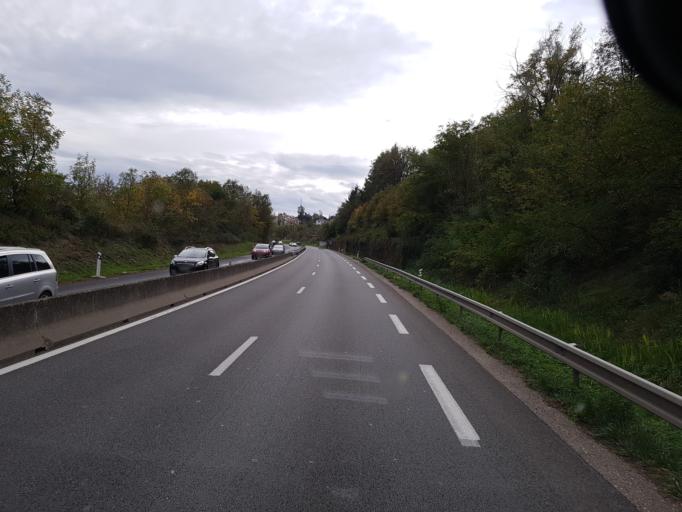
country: FR
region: Rhone-Alpes
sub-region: Departement de la Loire
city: Saint-Genest-Lerpt
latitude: 45.4487
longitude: 4.3372
